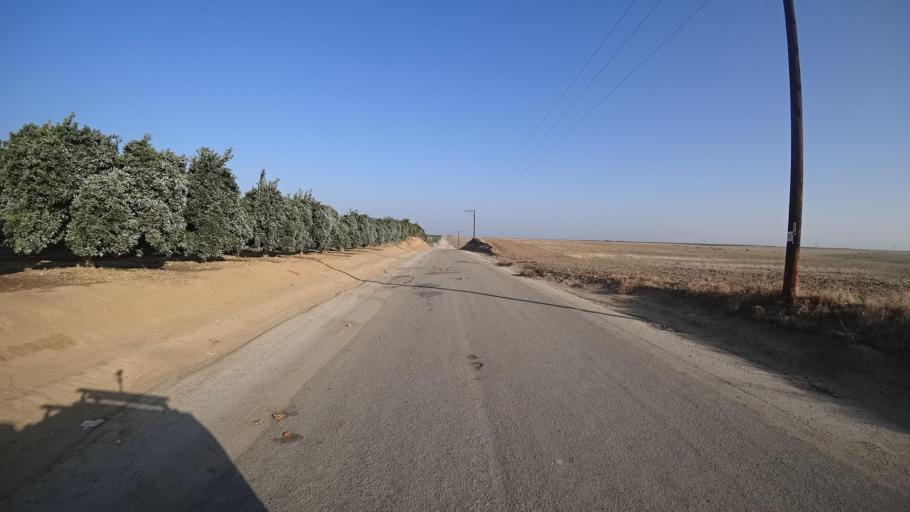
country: US
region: California
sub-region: Tulare County
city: Richgrove
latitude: 35.7672
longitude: -119.0807
